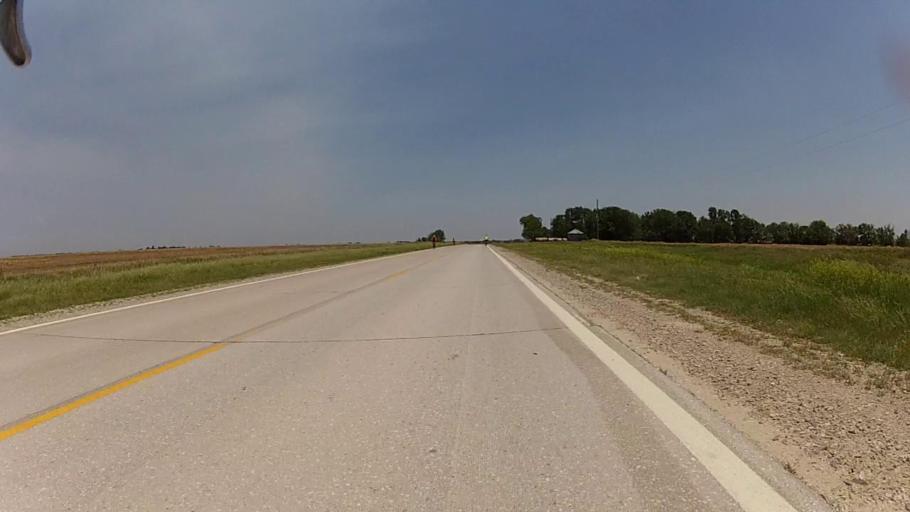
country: US
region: Kansas
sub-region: Sumner County
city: Wellington
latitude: 37.0575
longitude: -97.3576
